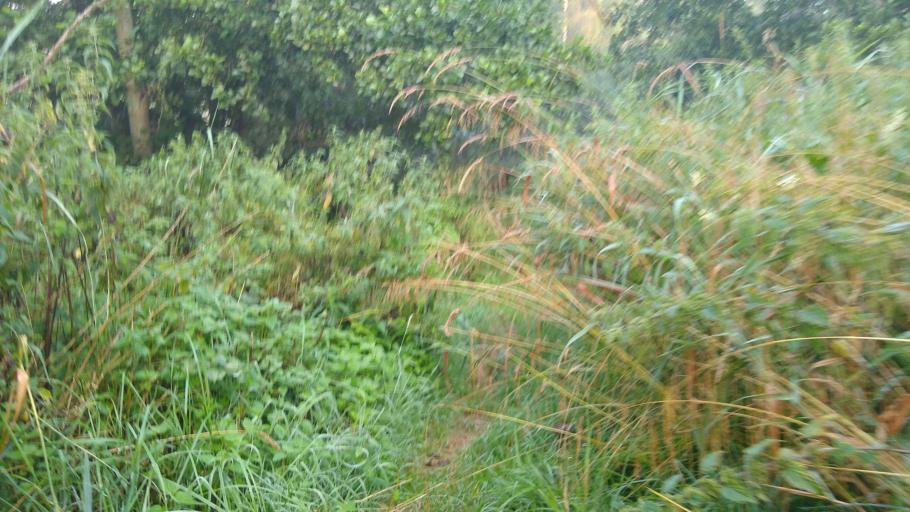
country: DK
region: South Denmark
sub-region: Fredericia Kommune
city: Fredericia
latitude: 55.6048
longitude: 9.7138
